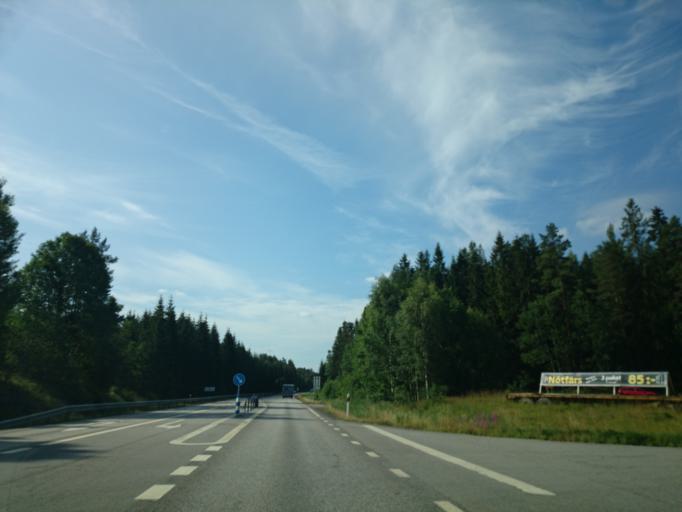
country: SE
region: OEstergoetland
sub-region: Valdemarsviks Kommun
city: Valdemarsvik
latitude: 58.1853
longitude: 16.5359
